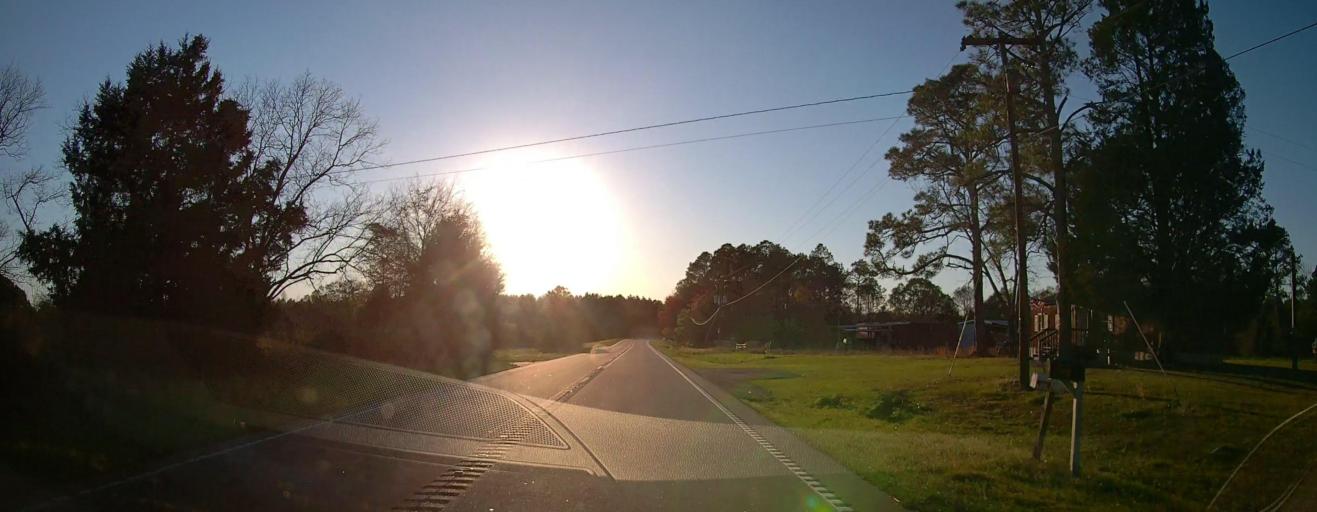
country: US
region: Georgia
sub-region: Wilcox County
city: Rochelle
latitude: 31.9449
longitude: -83.5492
